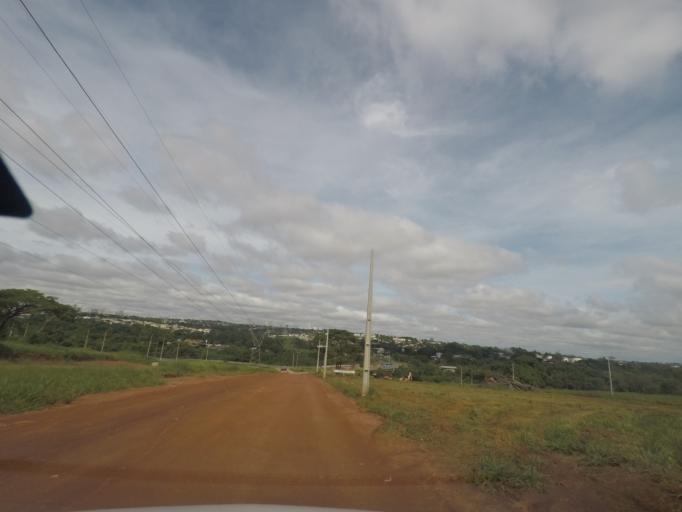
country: BR
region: Goias
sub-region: Goiania
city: Goiania
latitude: -16.6752
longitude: -49.1942
